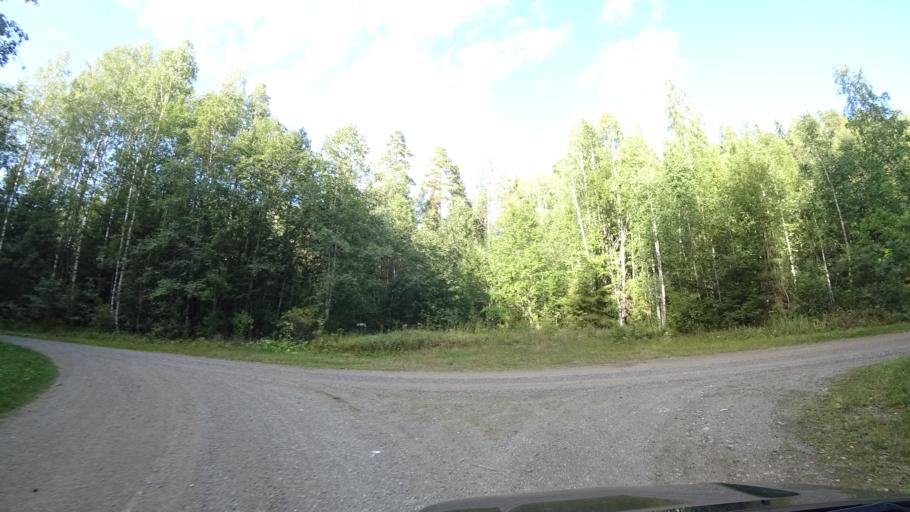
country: FI
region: Paijanne Tavastia
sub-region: Lahti
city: Auttoinen
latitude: 61.2255
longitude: 25.1938
